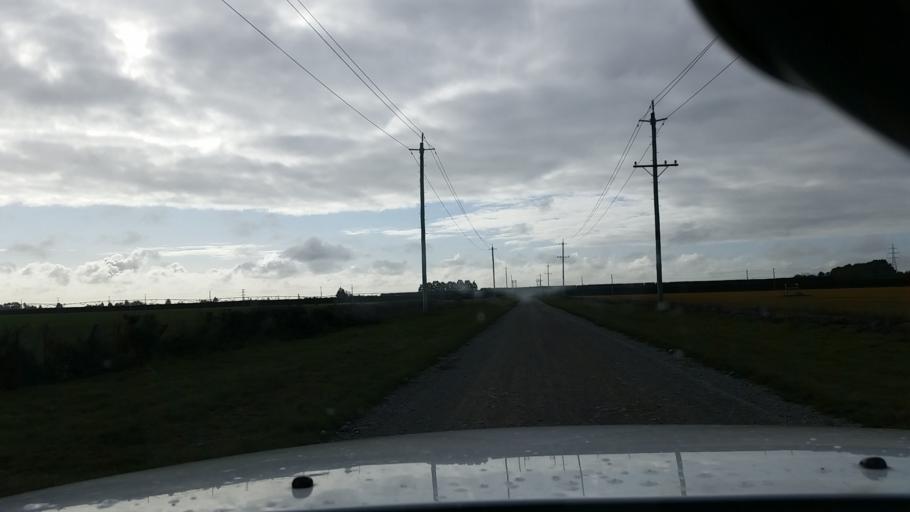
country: NZ
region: Canterbury
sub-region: Ashburton District
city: Ashburton
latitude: -43.9430
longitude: 171.7938
